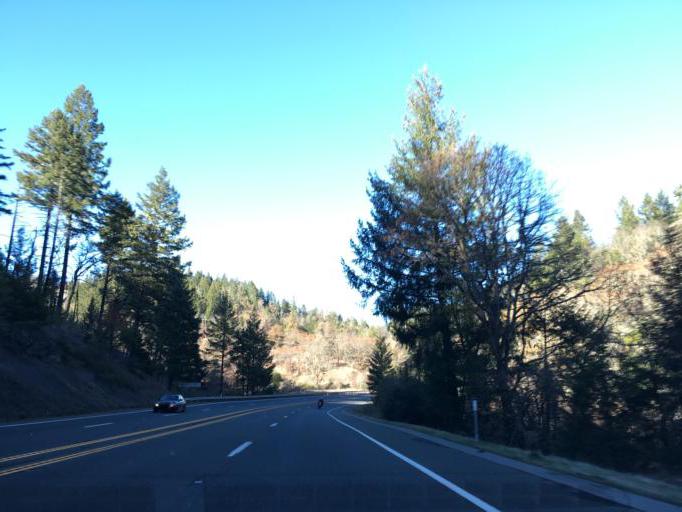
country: US
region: California
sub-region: Mendocino County
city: Laytonville
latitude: 39.5977
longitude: -123.4544
